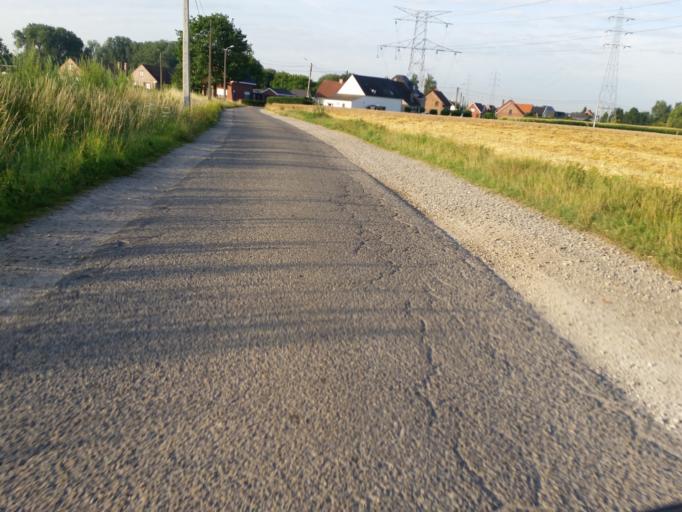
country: BE
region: Flanders
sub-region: Provincie Vlaams-Brabant
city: Zemst
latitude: 50.9646
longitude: 4.4296
